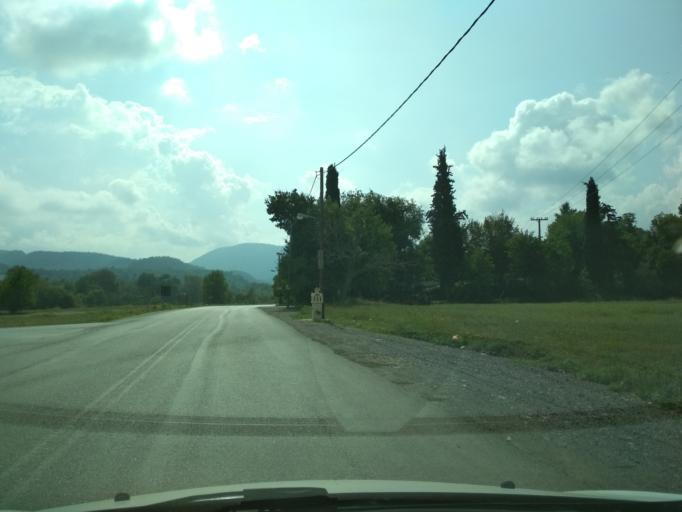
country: GR
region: Central Greece
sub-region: Nomos Evvoias
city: Prokopion
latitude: 38.7337
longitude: 23.4951
